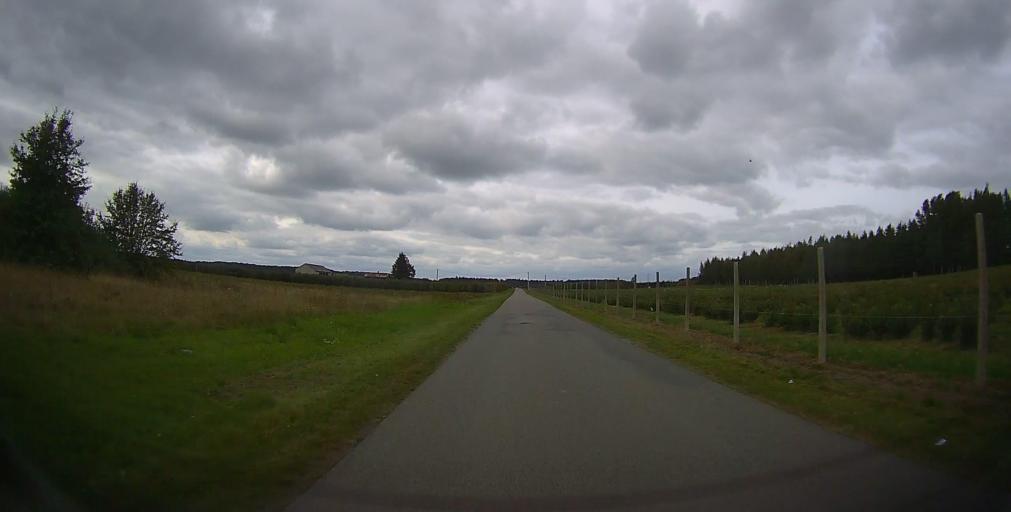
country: PL
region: Masovian Voivodeship
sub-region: Powiat grojecki
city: Goszczyn
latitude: 51.7621
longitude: 20.8703
